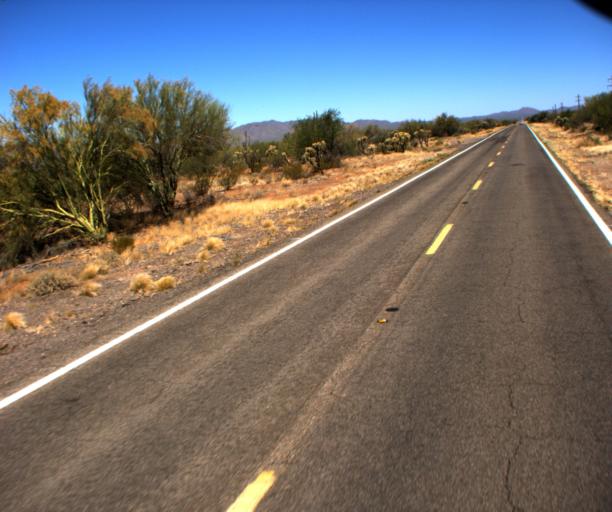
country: US
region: Arizona
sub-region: Pima County
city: Sells
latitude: 32.0488
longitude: -112.0243
